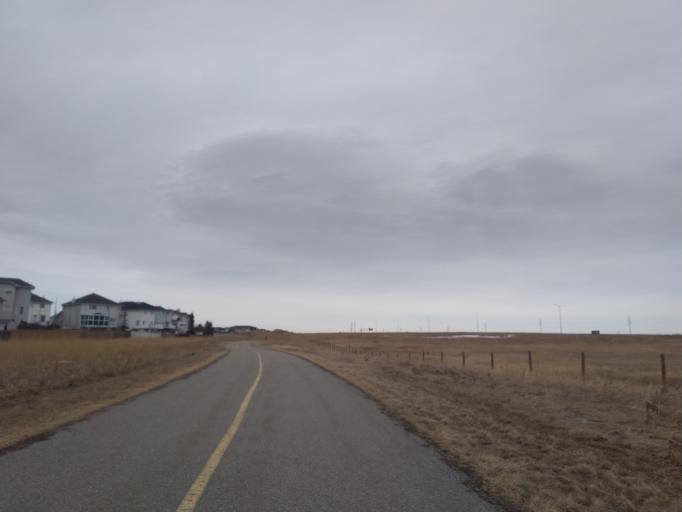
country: CA
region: Alberta
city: Chestermere
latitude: 51.1066
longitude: -113.9224
